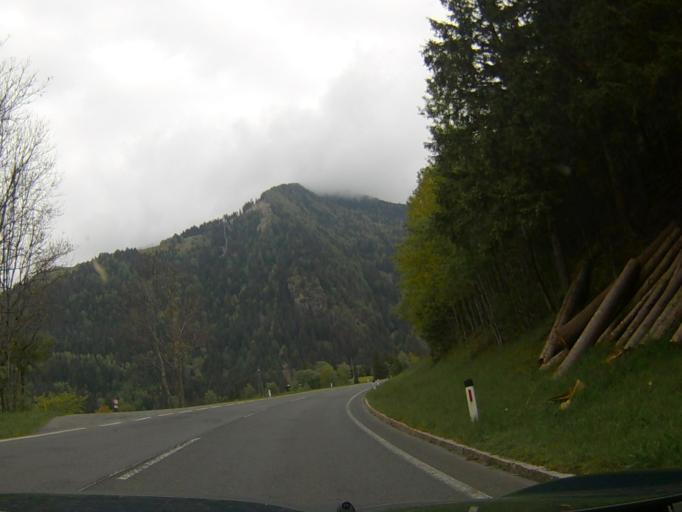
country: AT
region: Carinthia
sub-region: Politischer Bezirk Spittal an der Drau
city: Obervellach
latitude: 46.9440
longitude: 13.1861
